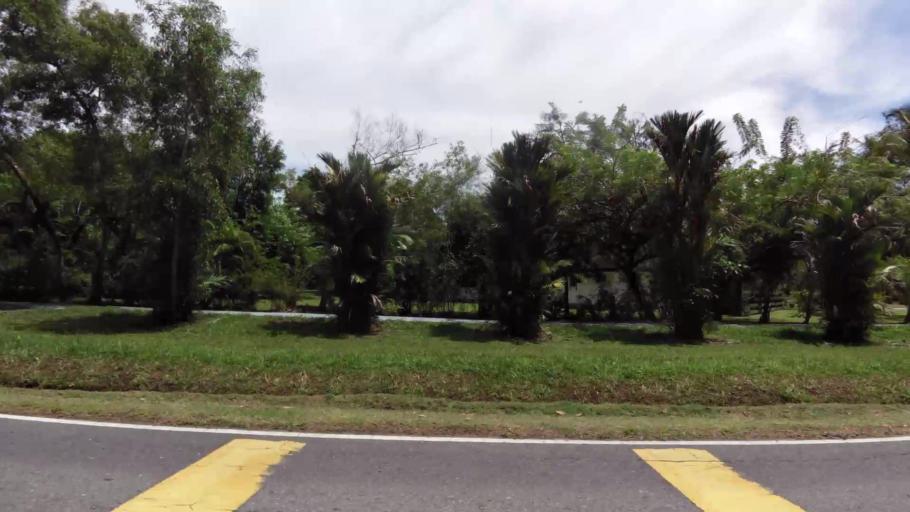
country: BN
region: Belait
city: Seria
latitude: 4.6041
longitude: 114.2836
